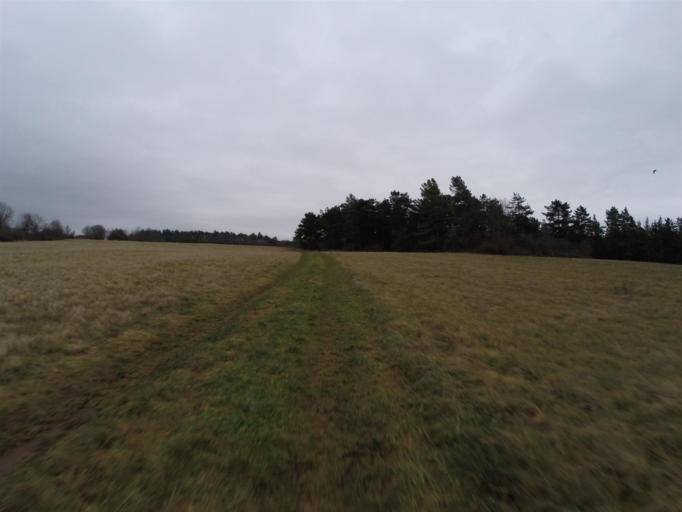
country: DE
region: Thuringia
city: Jena
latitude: 50.9135
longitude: 11.6201
